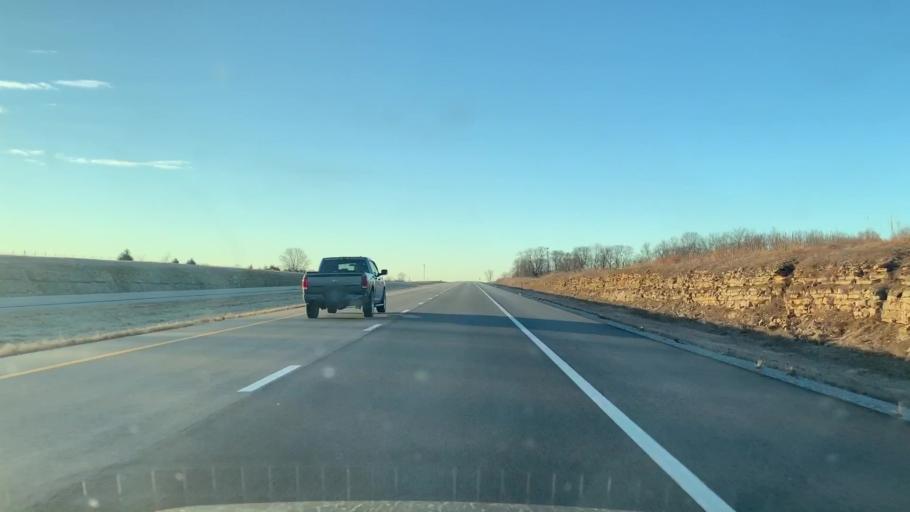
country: US
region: Kansas
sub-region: Linn County
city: La Cygne
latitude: 38.3859
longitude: -94.6878
